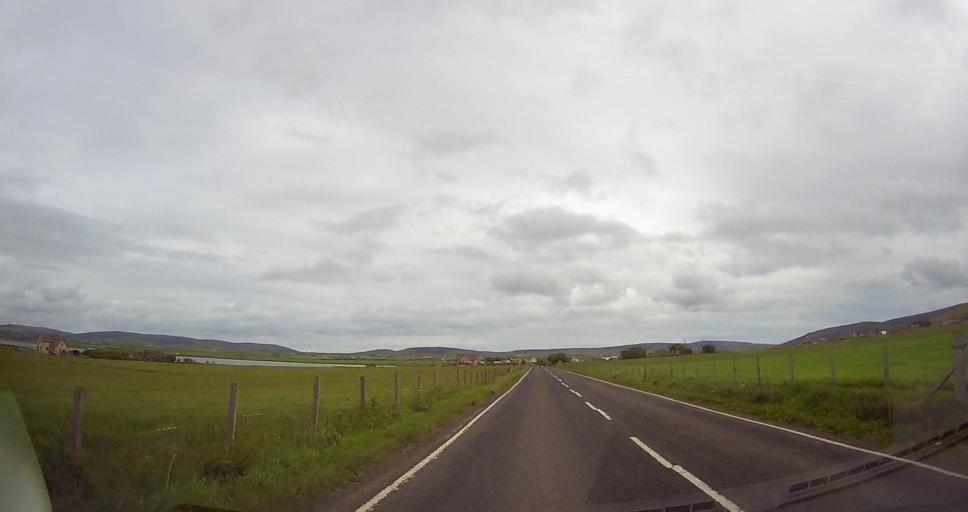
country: GB
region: Scotland
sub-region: Orkney Islands
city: Stromness
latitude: 58.9861
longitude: -3.2237
